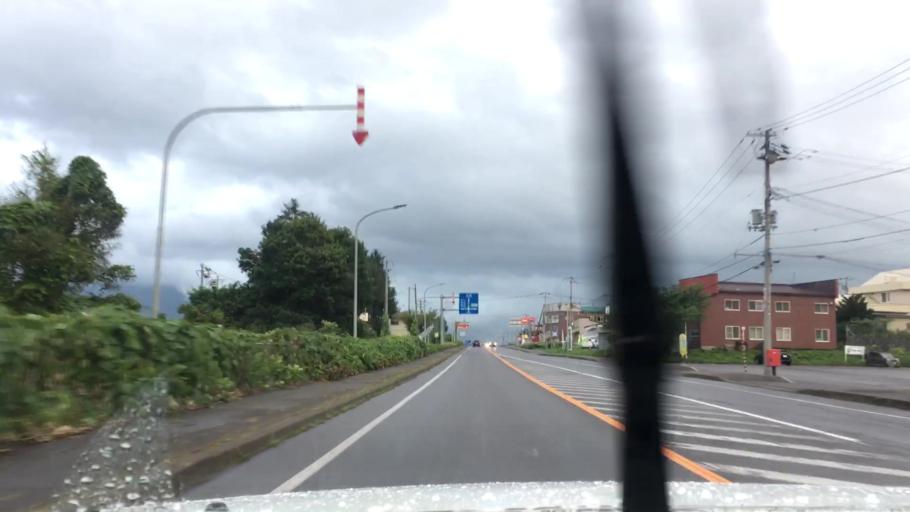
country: JP
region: Hokkaido
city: Nanae
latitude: 42.0957
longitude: 140.5725
